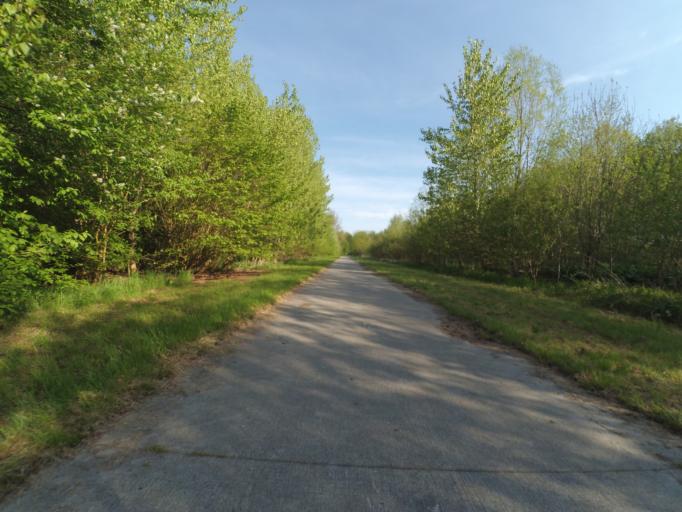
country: NL
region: North Holland
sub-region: Gemeente Huizen
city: Huizen
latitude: 52.3400
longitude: 5.2941
